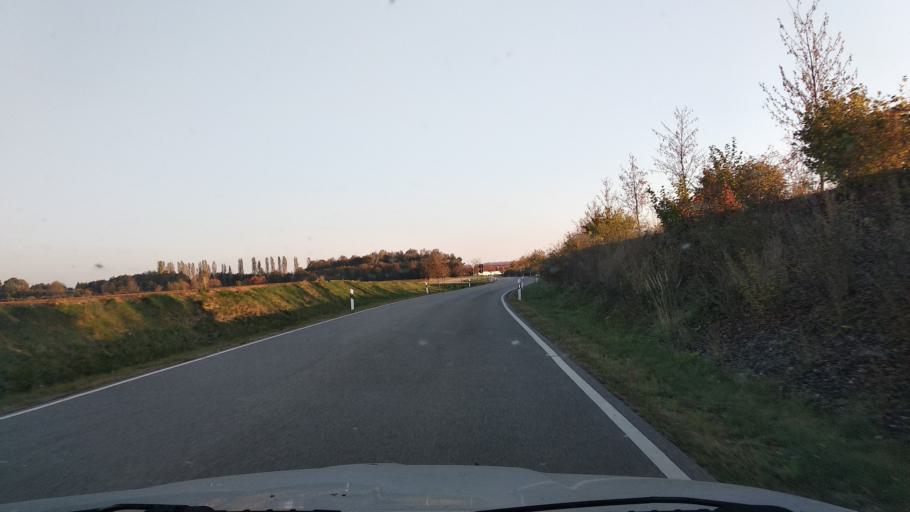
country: DE
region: Bavaria
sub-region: Upper Bavaria
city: Aschheim
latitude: 48.1697
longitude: 11.7270
